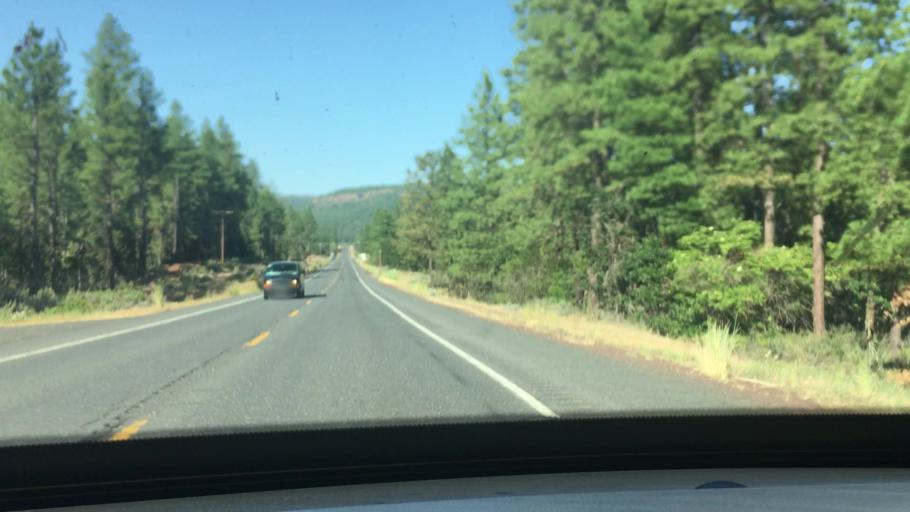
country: US
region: Washington
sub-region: Klickitat County
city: Goldendale
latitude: 45.9382
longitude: -120.6864
